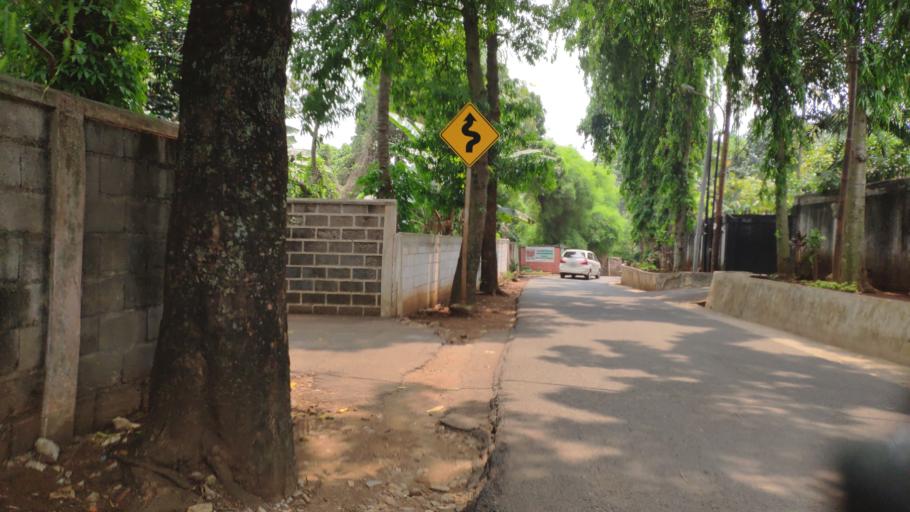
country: ID
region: West Java
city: Depok
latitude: -6.3190
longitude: 106.8316
